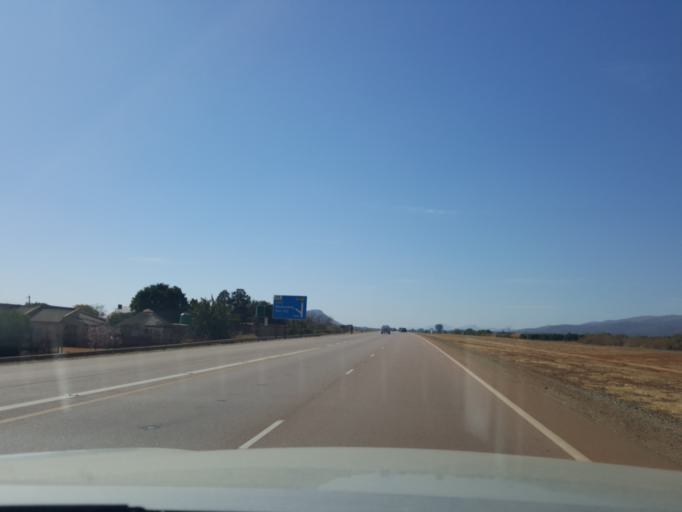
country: ZA
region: North-West
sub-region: Bojanala Platinum District Municipality
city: Brits
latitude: -25.7357
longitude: 27.6454
